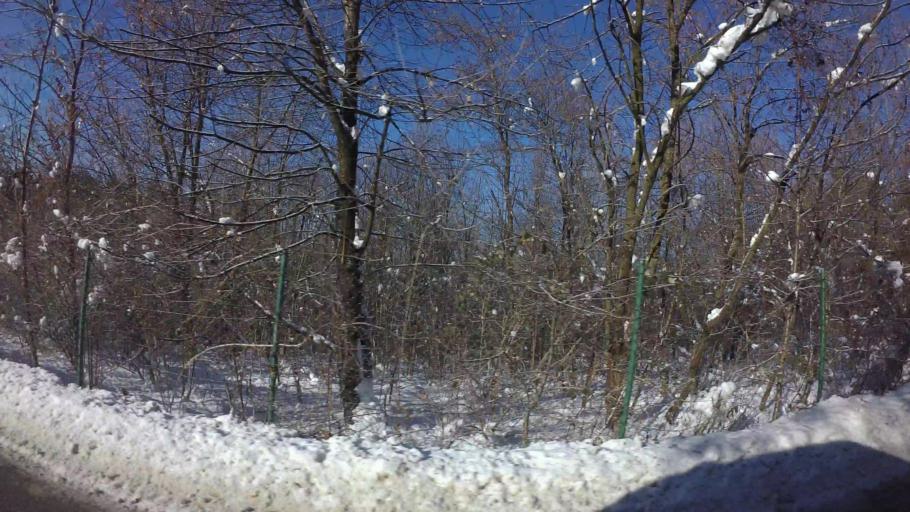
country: BA
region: Federation of Bosnia and Herzegovina
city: Kobilja Glava
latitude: 43.8882
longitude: 18.4098
